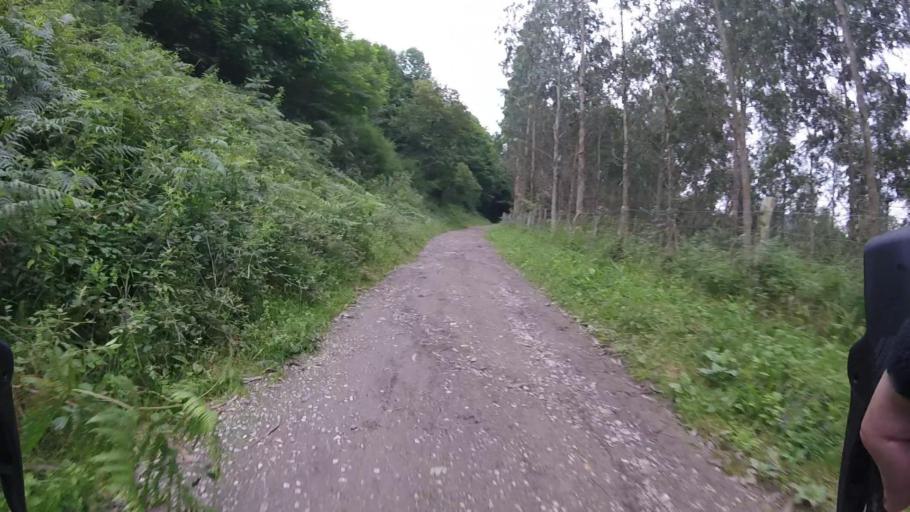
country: ES
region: Basque Country
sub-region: Provincia de Guipuzcoa
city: Errenteria
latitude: 43.2580
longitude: -1.8886
